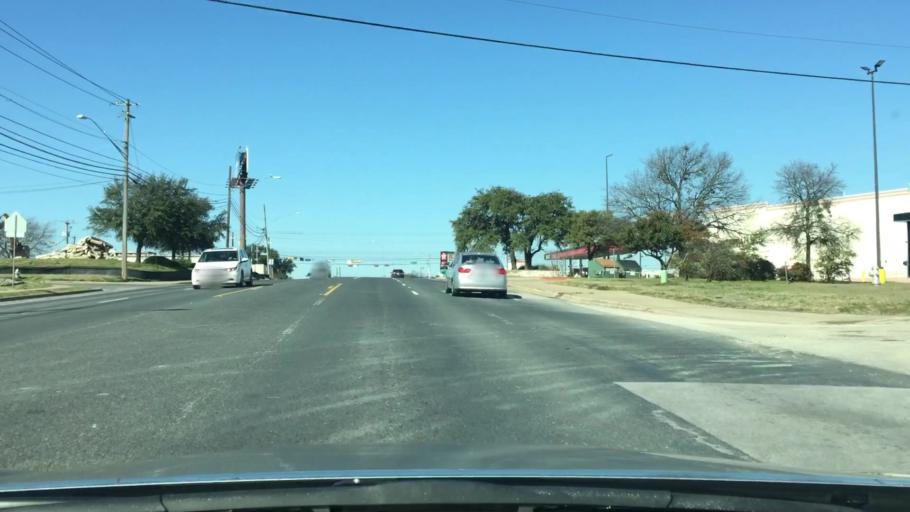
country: US
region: Texas
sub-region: Travis County
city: Wells Branch
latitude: 30.3809
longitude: -97.6847
